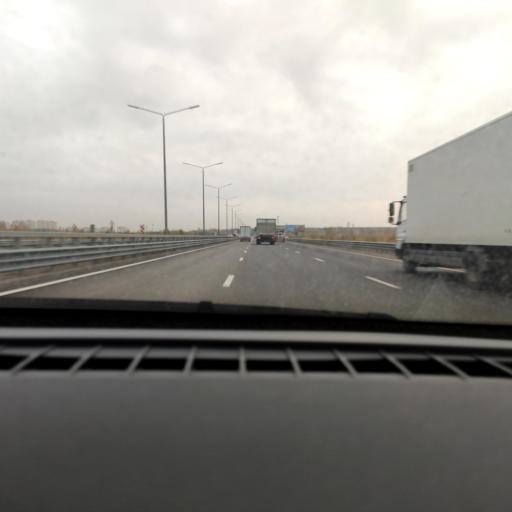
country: RU
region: Voronezj
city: Somovo
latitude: 51.7570
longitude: 39.3068
